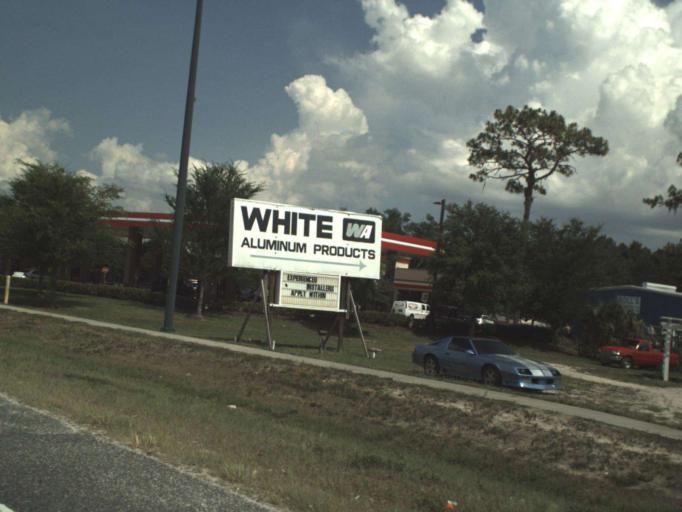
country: US
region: Florida
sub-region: Lake County
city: Leesburg
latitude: 28.8188
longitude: -81.8405
